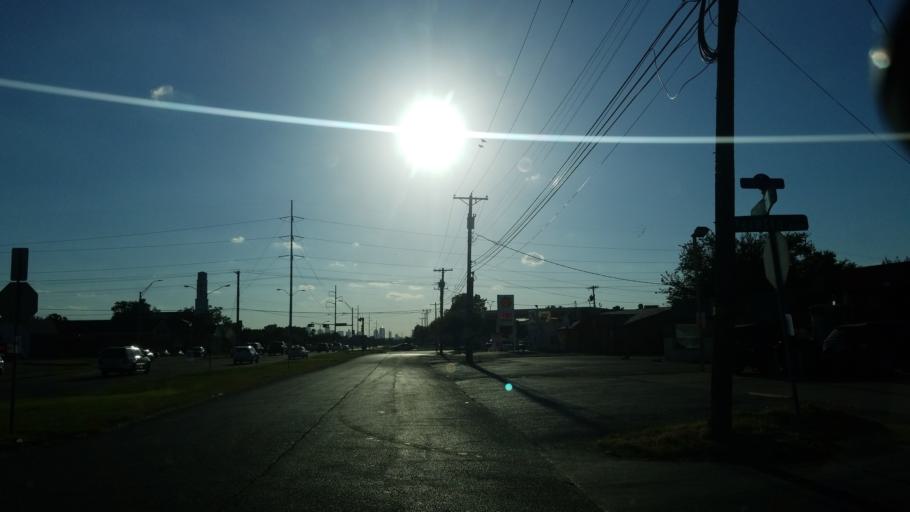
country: US
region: Texas
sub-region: Dallas County
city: Balch Springs
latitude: 32.7726
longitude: -96.6987
